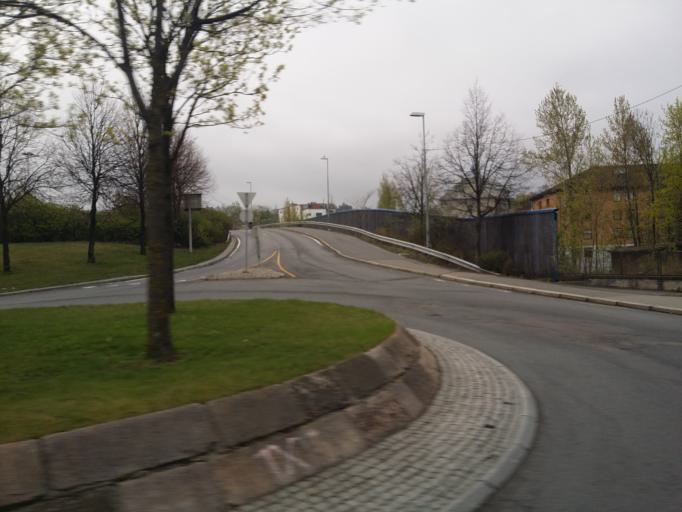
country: NO
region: Oslo
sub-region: Oslo
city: Oslo
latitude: 59.9103
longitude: 10.7920
